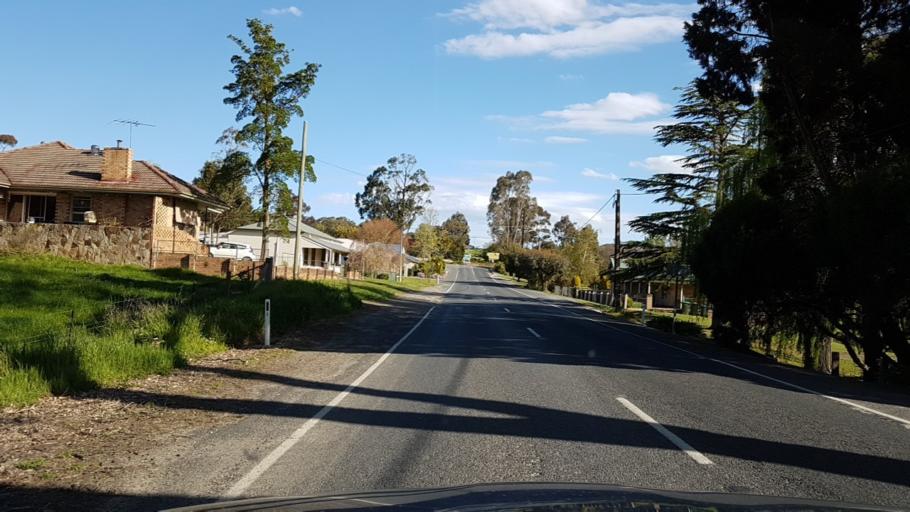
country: AU
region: South Australia
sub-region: Adelaide Hills
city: Lobethal
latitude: -34.8946
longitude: 138.8795
